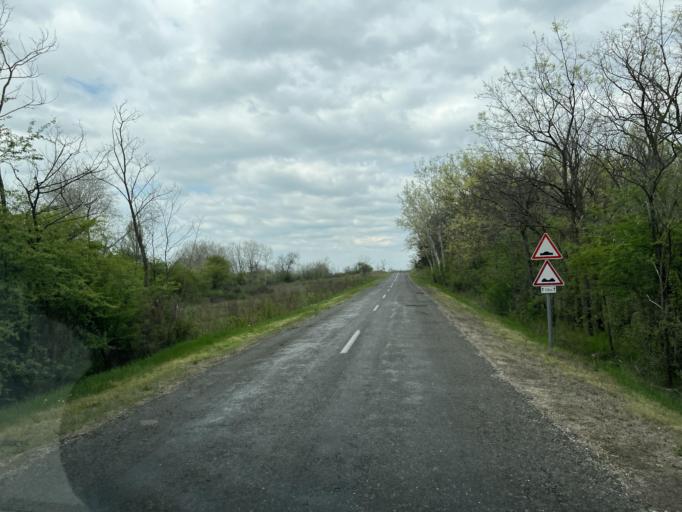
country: HU
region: Pest
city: Dabas
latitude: 47.1220
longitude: 19.3530
